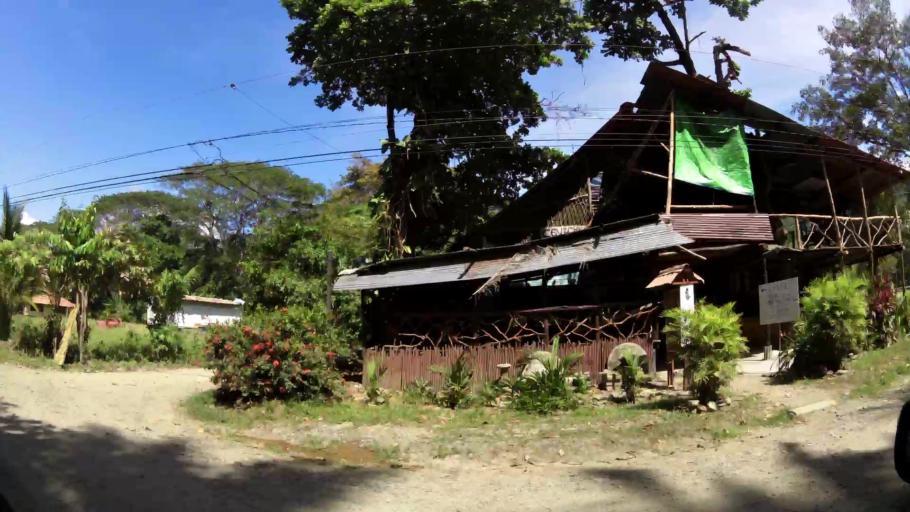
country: CR
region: San Jose
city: San Isidro
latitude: 9.2508
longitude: -83.8627
